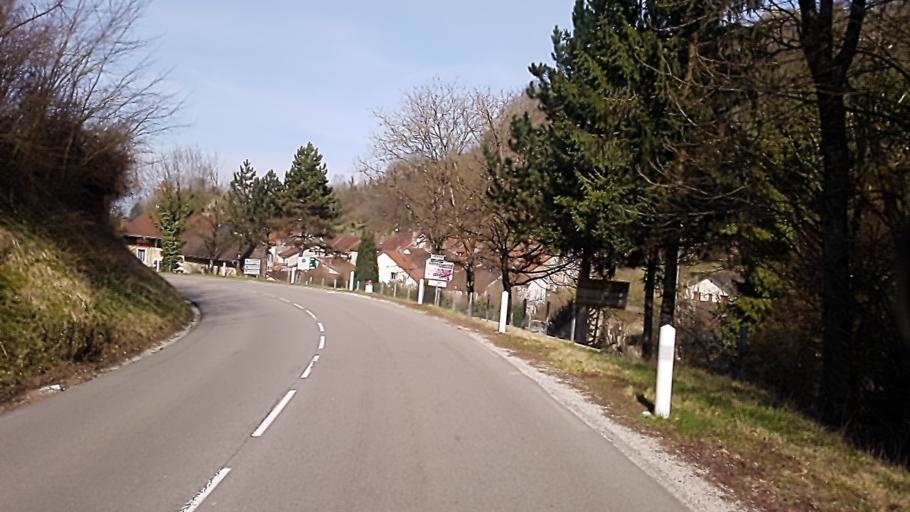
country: FR
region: Franche-Comte
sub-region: Departement du Jura
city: Poligny
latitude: 46.8322
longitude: 5.7143
